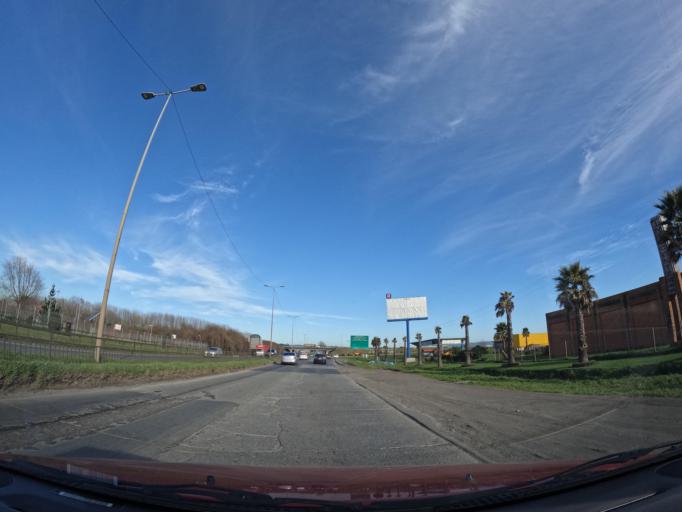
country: CL
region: Biobio
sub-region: Provincia de Concepcion
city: Concepcion
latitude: -36.7829
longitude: -73.0756
